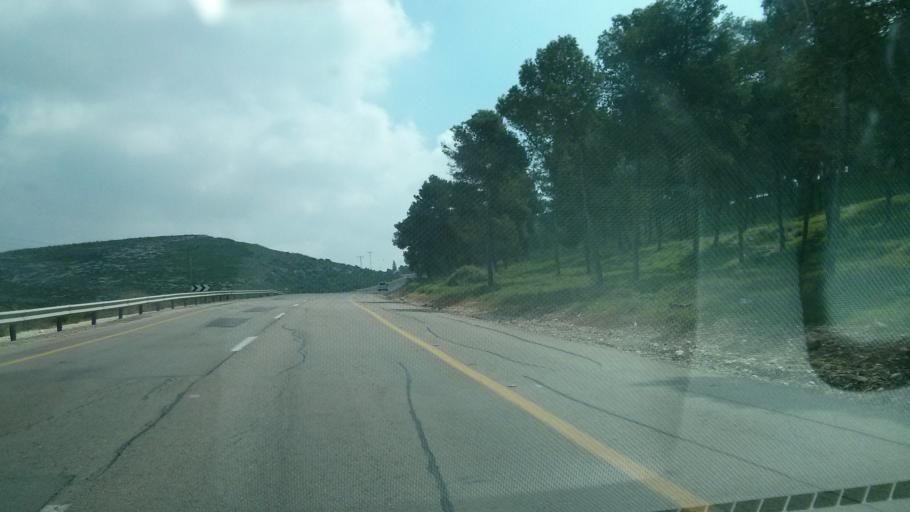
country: IL
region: Southern District
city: Lehavim
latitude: 31.3859
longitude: 34.8621
